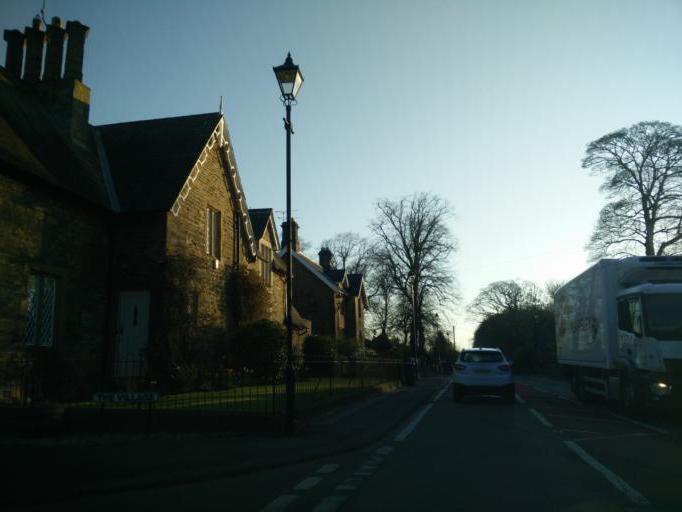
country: GB
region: England
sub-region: County Durham
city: Ushaw Moor
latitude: 54.7363
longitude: -1.6569
